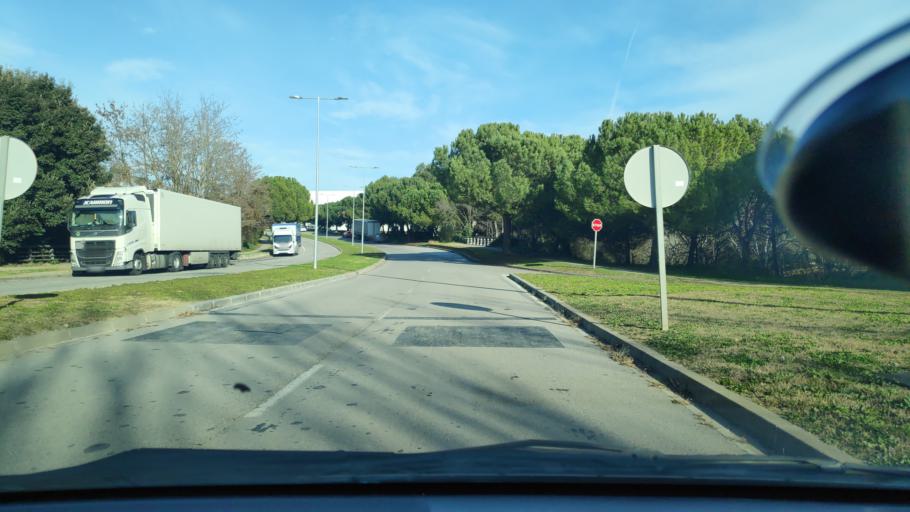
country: ES
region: Catalonia
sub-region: Provincia de Barcelona
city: Rubi
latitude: 41.4856
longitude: 2.0455
